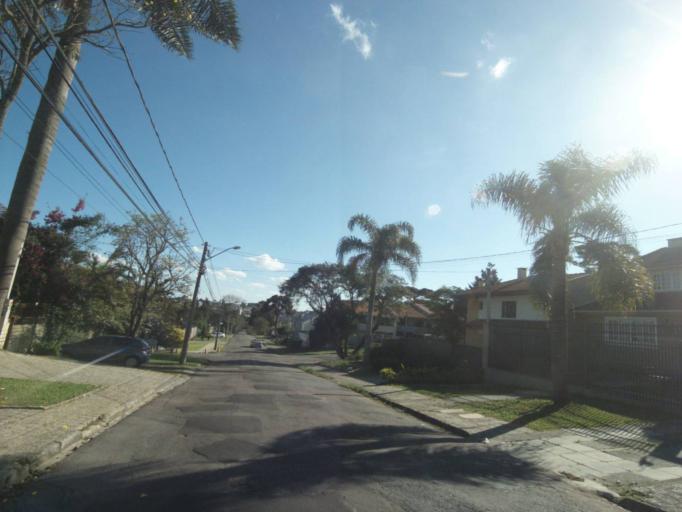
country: BR
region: Parana
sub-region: Curitiba
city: Curitiba
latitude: -25.3799
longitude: -49.2433
